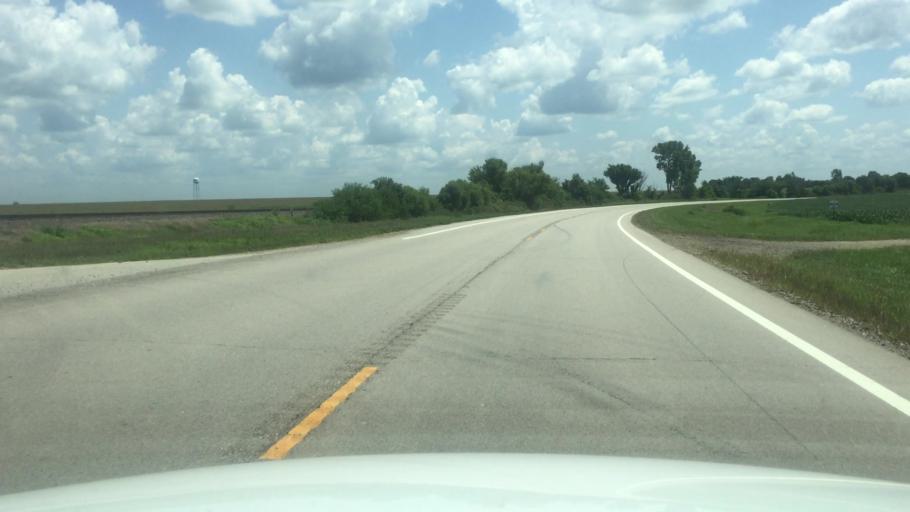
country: US
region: Kansas
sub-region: Brown County
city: Horton
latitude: 39.6506
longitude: -95.3587
